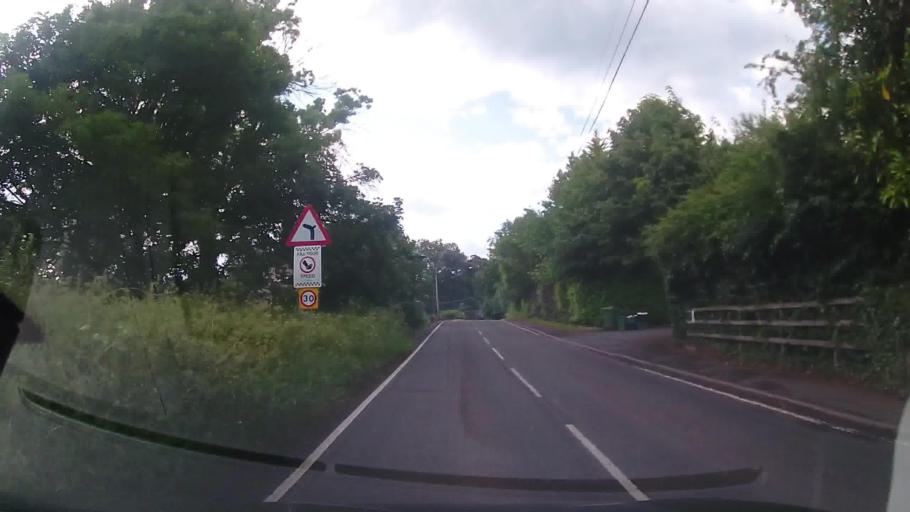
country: GB
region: England
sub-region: Shropshire
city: Harley
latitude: 52.6458
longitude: -2.5767
